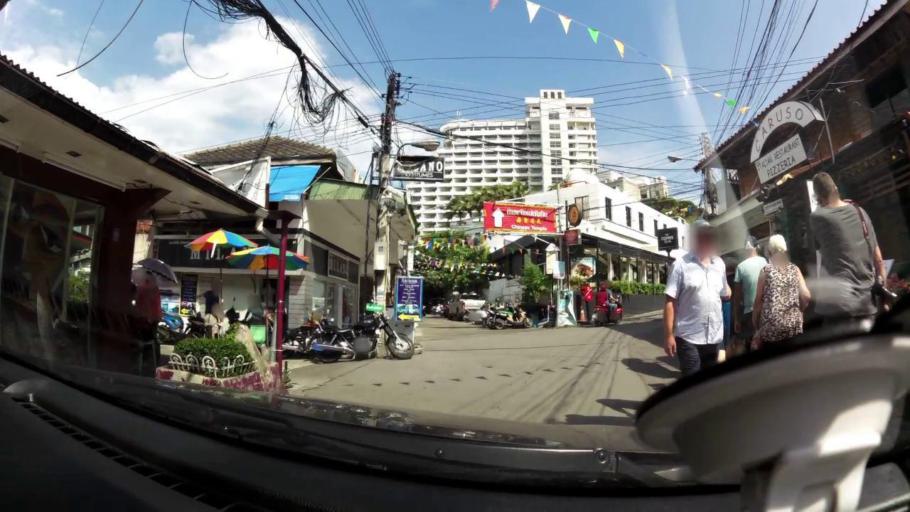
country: TH
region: Prachuap Khiri Khan
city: Hua Hin
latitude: 12.5719
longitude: 99.9602
